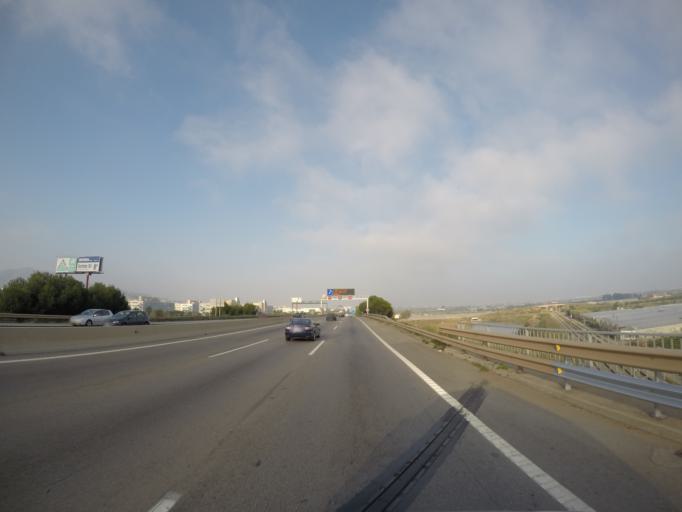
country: ES
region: Catalonia
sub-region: Provincia de Barcelona
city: Viladecans
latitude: 41.3108
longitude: 2.0310
